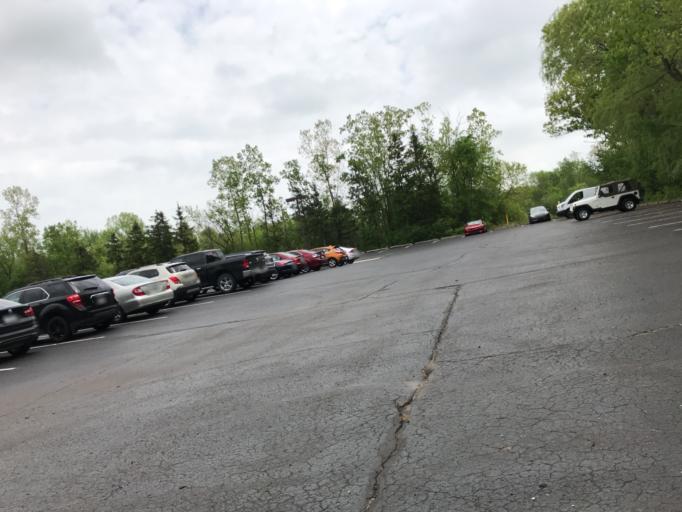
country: US
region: Michigan
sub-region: Oakland County
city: West Bloomfield Township
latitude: 42.5325
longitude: -83.3586
